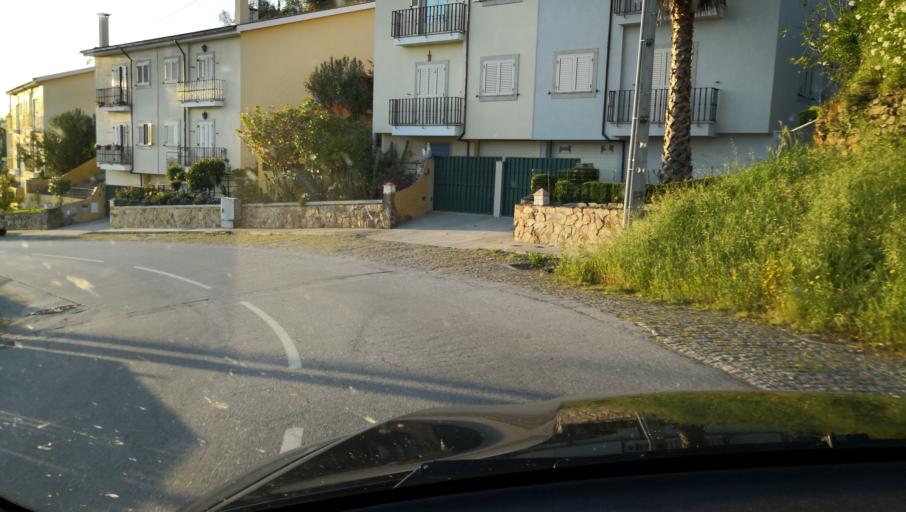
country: PT
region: Vila Real
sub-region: Mondim de Basto
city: Mondim de Basto
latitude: 41.4089
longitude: -7.9449
